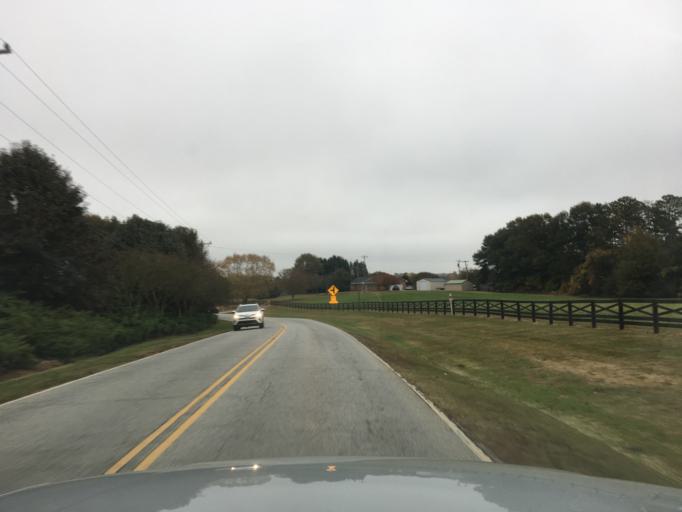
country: US
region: South Carolina
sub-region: Greenville County
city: Five Forks
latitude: 34.8483
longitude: -82.2652
